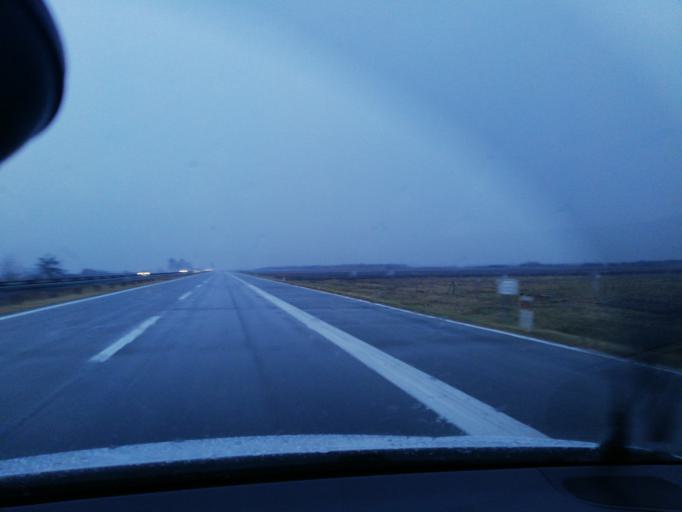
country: RS
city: Sasinci
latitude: 44.9770
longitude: 19.7416
